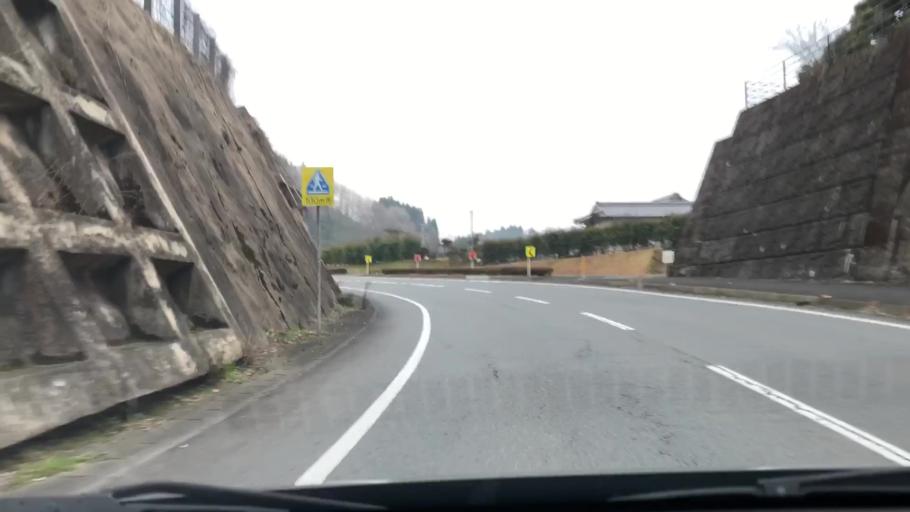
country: JP
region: Oita
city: Takedamachi
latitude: 32.9791
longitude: 131.5476
